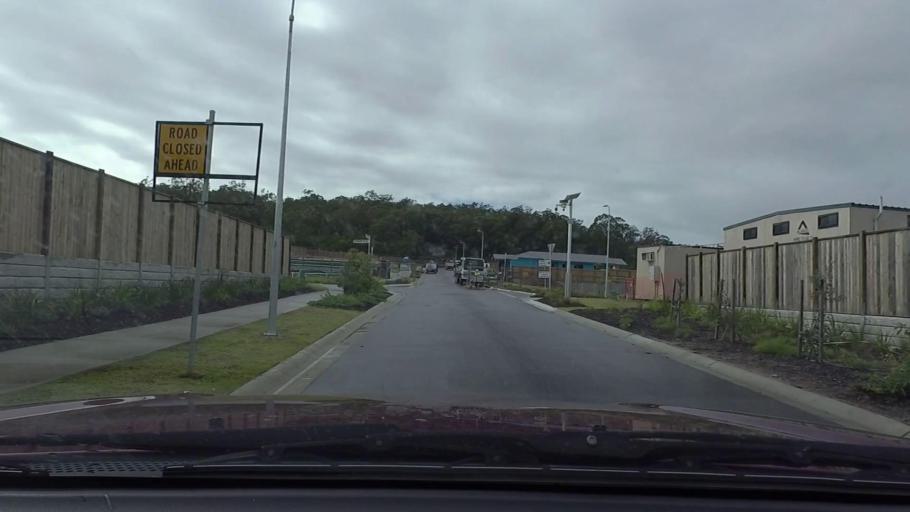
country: AU
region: Queensland
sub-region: Logan
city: Chambers Flat
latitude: -27.8164
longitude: 153.1313
